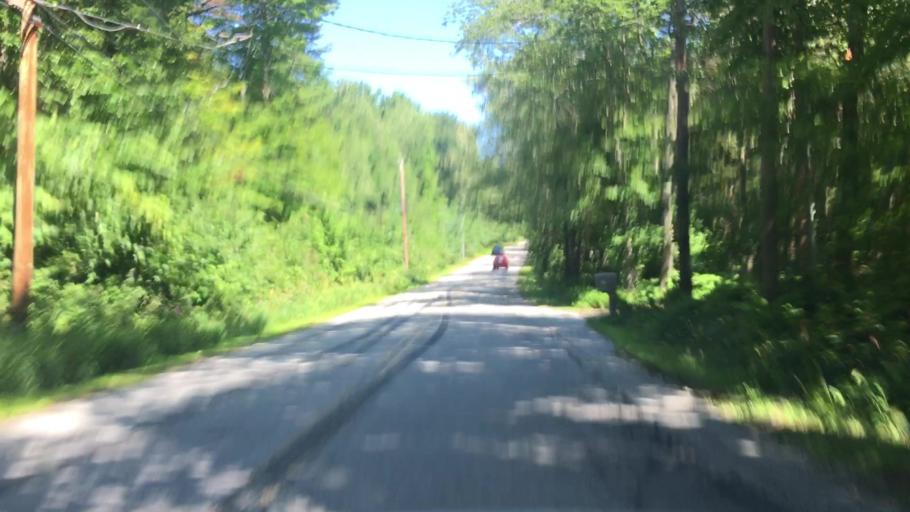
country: US
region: New Hampshire
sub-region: Merrimack County
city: South Hooksett
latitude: 43.0329
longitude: -71.3875
